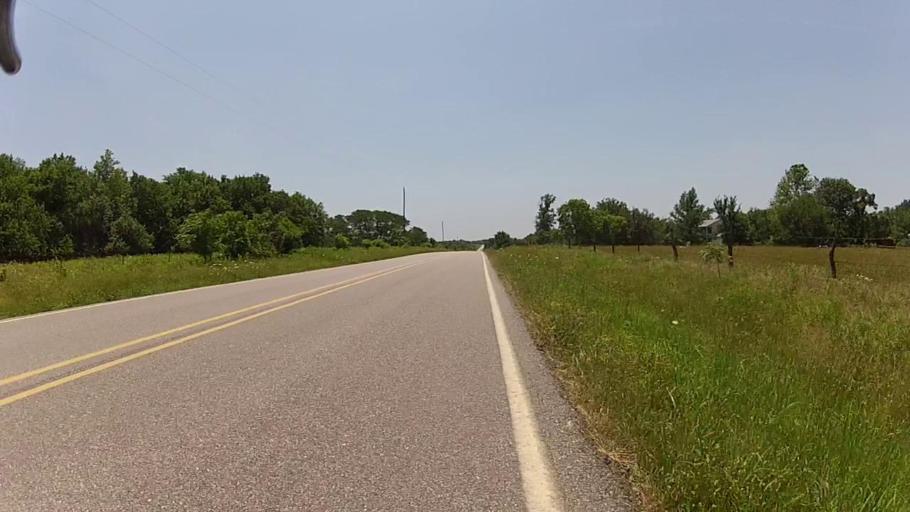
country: US
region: Kansas
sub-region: Montgomery County
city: Cherryvale
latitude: 37.2355
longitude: -95.5375
